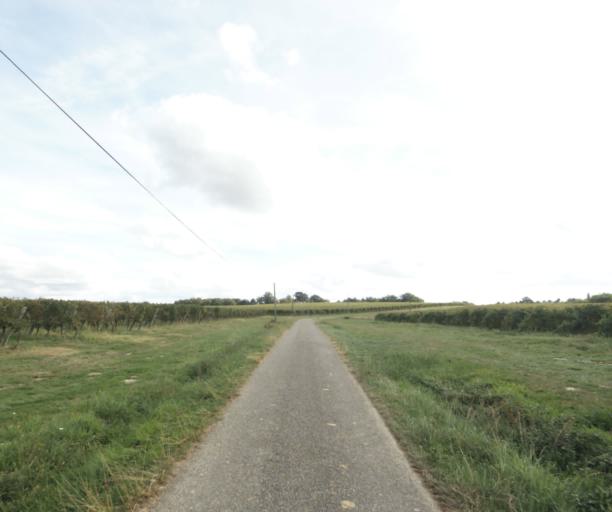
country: FR
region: Midi-Pyrenees
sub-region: Departement du Gers
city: Eauze
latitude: 43.8504
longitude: 0.1530
